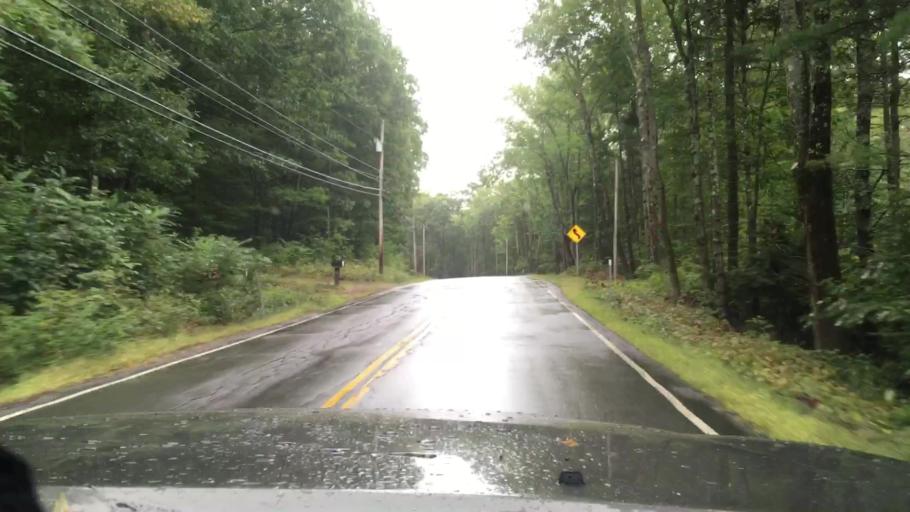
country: US
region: New Hampshire
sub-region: Belknap County
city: Meredith
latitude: 43.6487
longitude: -71.5417
